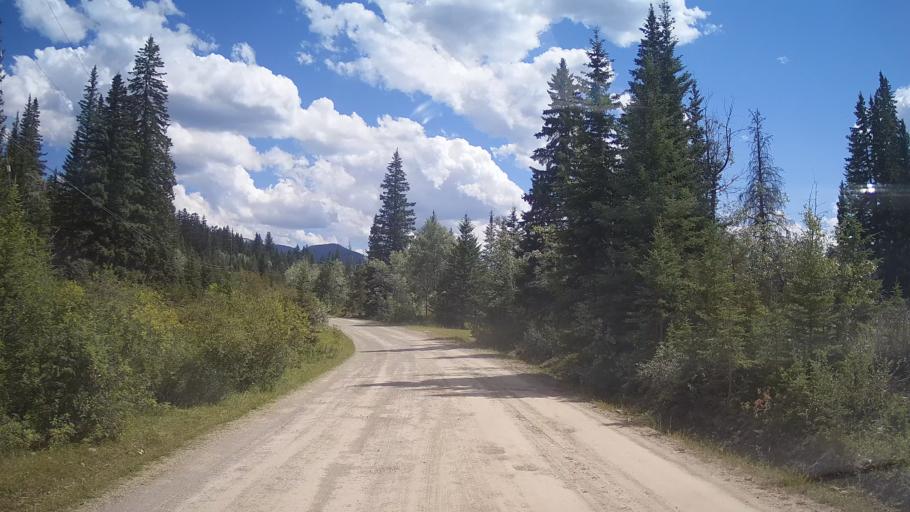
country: CA
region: British Columbia
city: Lillooet
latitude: 51.2928
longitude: -121.9792
